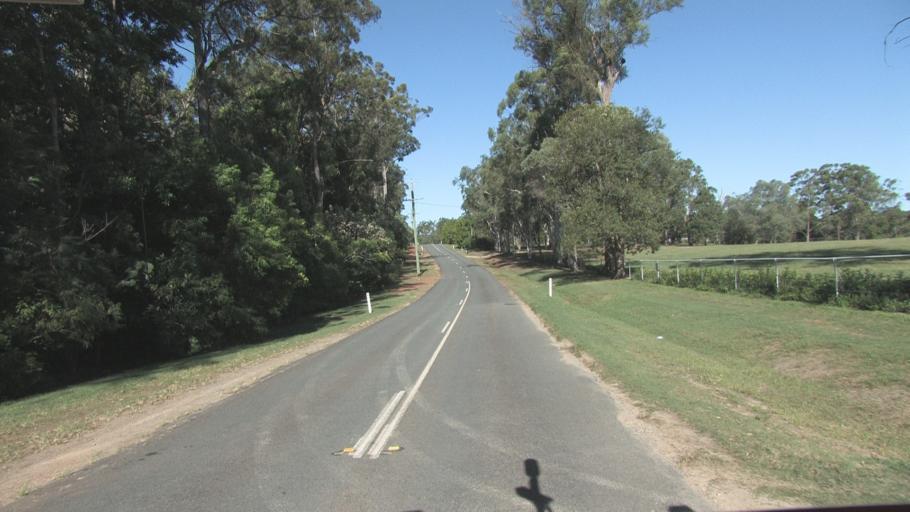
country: AU
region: Queensland
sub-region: Logan
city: Springwood
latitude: -27.5931
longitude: 153.1572
